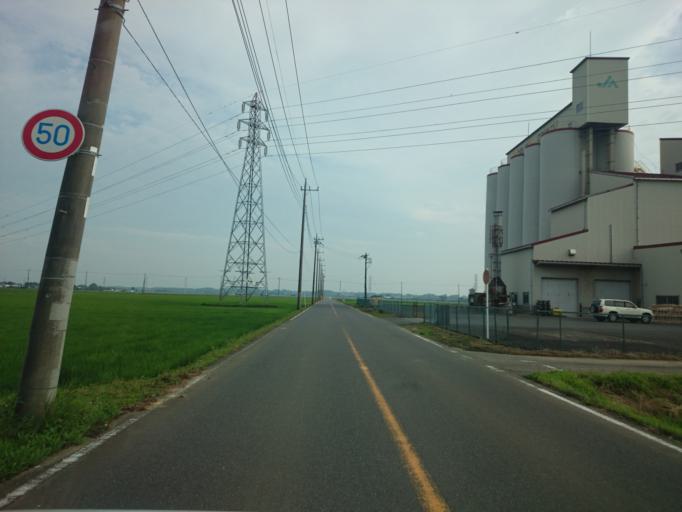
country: JP
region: Ibaraki
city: Tsukuba
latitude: 36.1662
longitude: 140.0989
